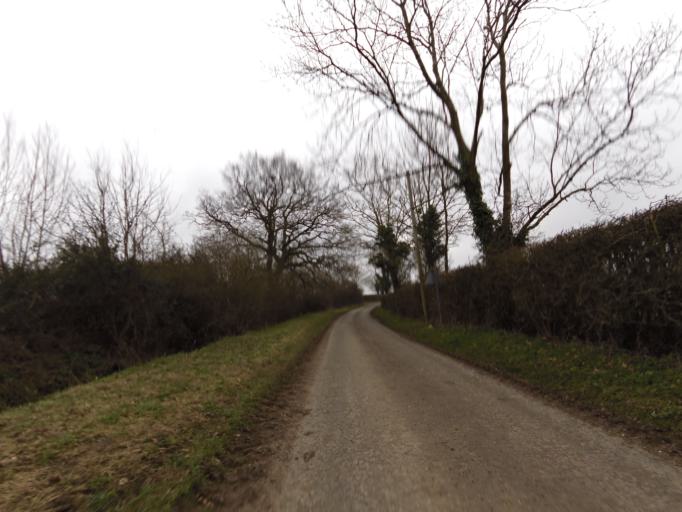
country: GB
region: England
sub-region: Suffolk
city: Framlingham
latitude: 52.2489
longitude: 1.4089
